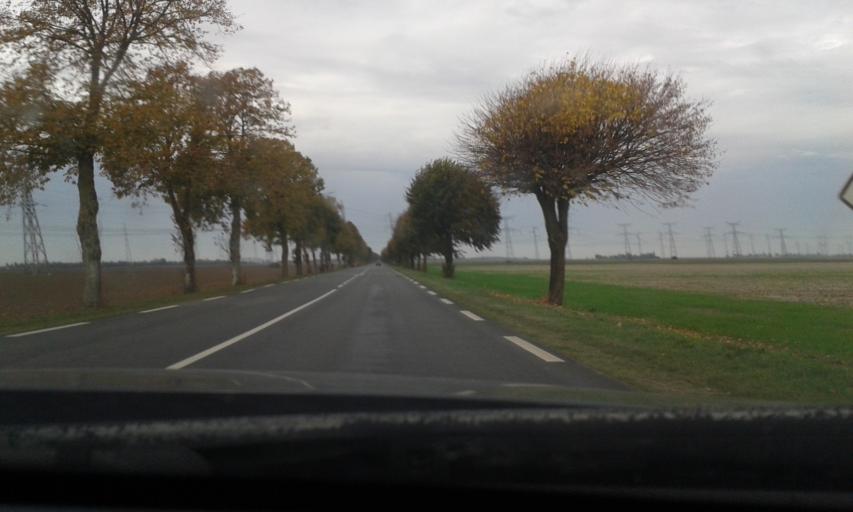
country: FR
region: Centre
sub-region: Departement du Loiret
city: Artenay
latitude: 48.1092
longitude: 1.8629
